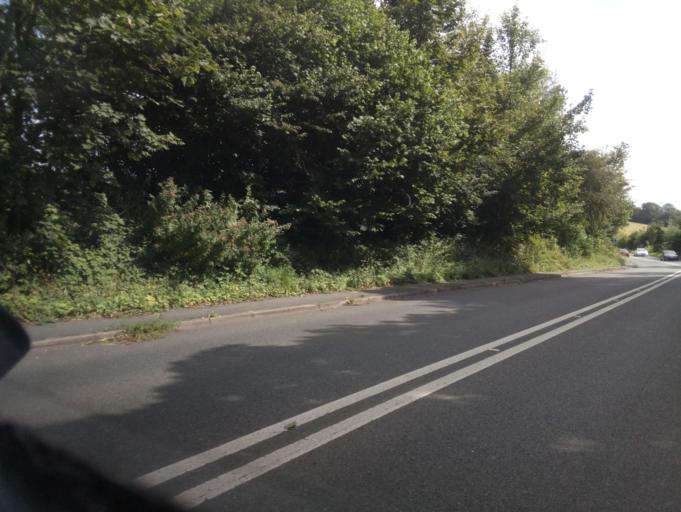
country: GB
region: England
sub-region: Borough of Torbay
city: Brixham
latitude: 50.3901
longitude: -3.5436
